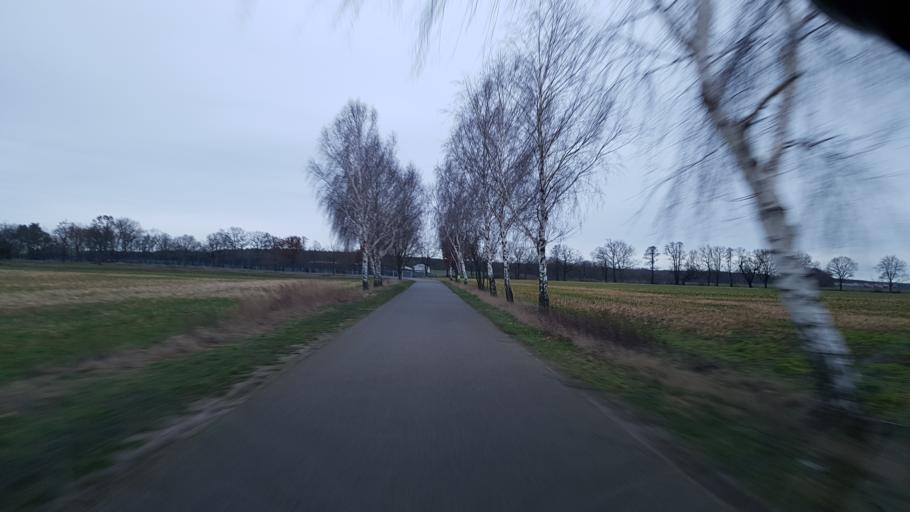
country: DE
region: Brandenburg
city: Schlieben
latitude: 51.7003
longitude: 13.3222
